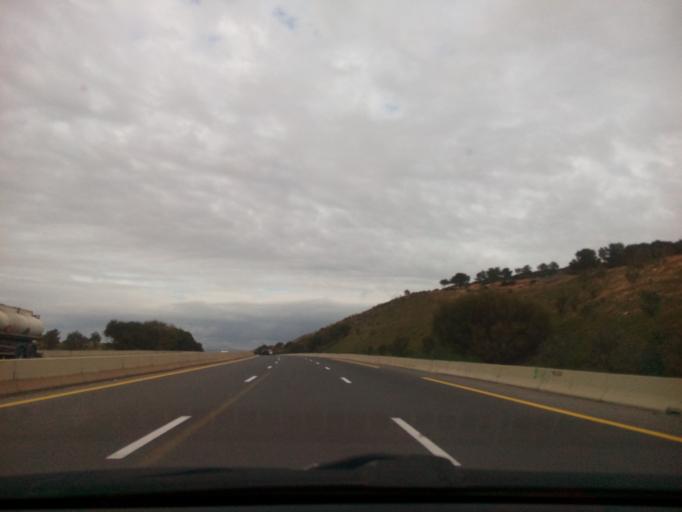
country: DZ
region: Sidi Bel Abbes
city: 'Ain el Berd
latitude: 35.4688
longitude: -0.3828
